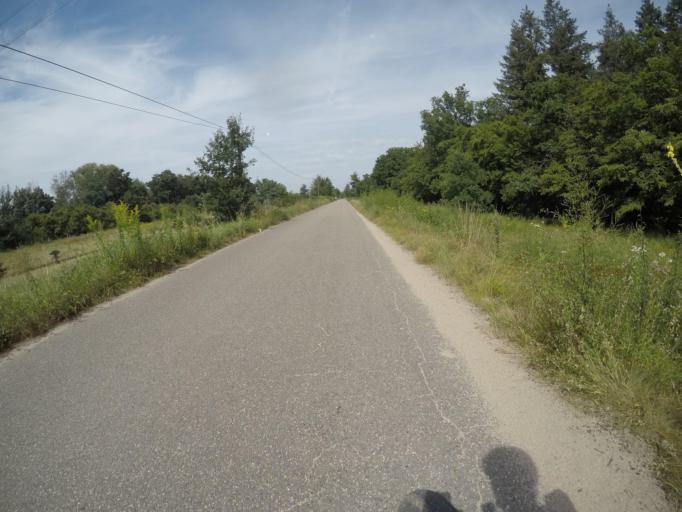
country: DE
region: Baden-Wuerttemberg
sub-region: Karlsruhe Region
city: Neulussheim
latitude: 49.2781
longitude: 8.5243
